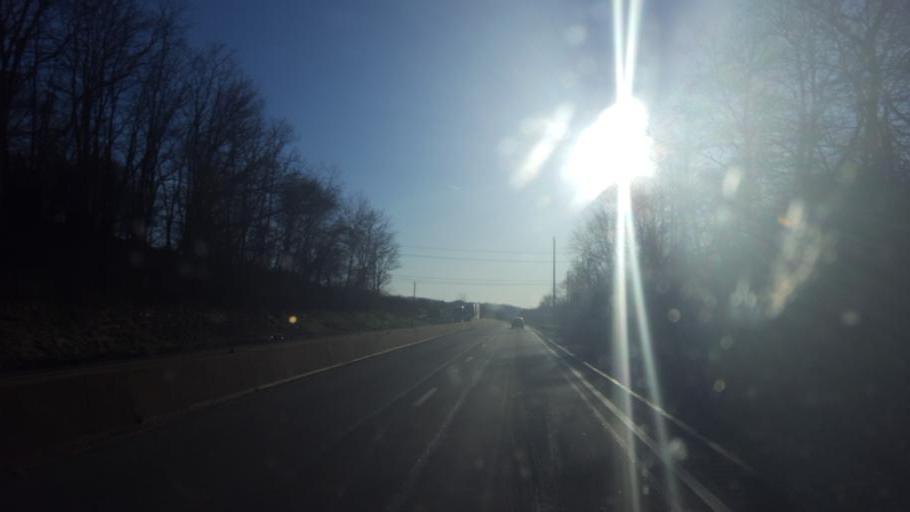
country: US
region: Pennsylvania
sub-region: Westmoreland County
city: New Stanton
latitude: 40.2159
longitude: -79.6356
